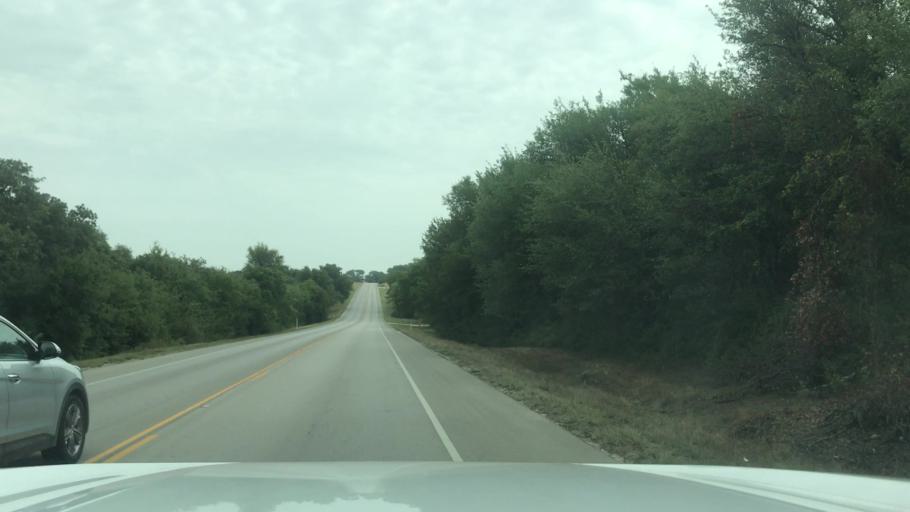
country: US
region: Texas
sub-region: Erath County
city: Dublin
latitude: 32.0963
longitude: -98.4059
